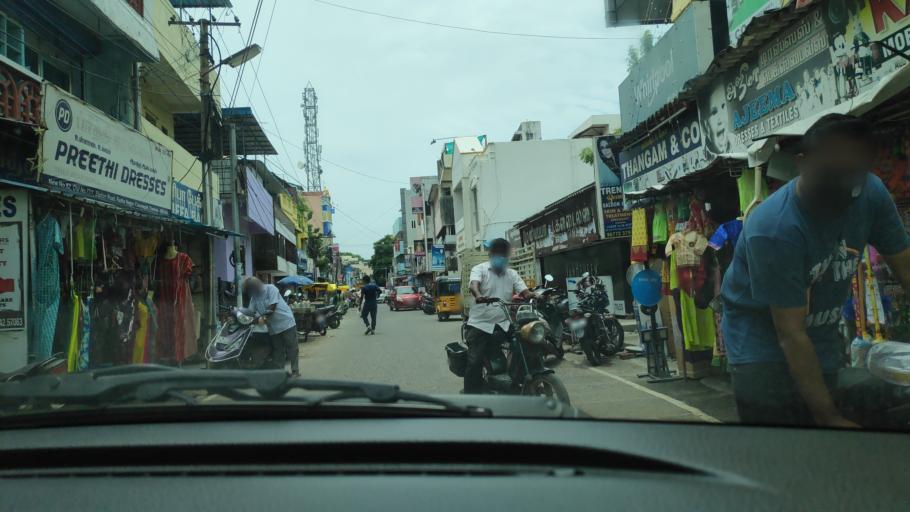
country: IN
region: Tamil Nadu
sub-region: Kancheepuram
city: Pallavaram
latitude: 12.9505
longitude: 80.1452
